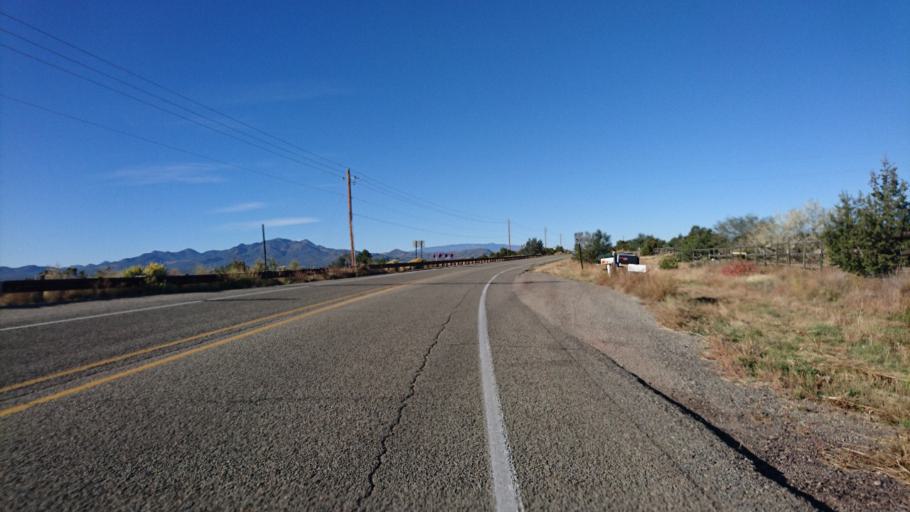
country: US
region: New Mexico
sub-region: Santa Fe County
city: La Cienega
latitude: 35.4531
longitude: -106.0712
